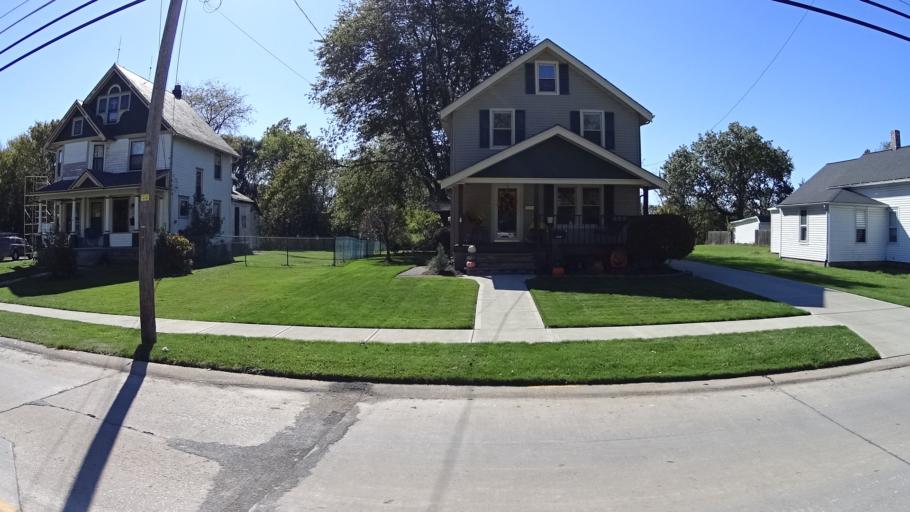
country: US
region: Ohio
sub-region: Lorain County
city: Amherst
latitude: 41.3911
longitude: -82.2205
